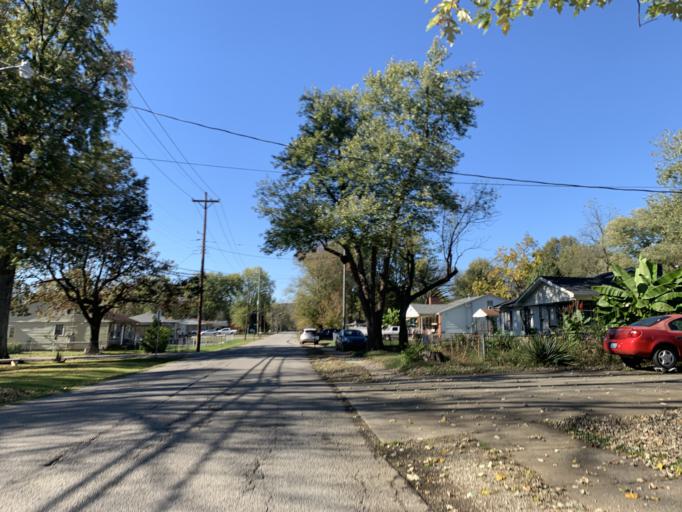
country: US
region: Kentucky
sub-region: Jefferson County
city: Saint Dennis
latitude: 38.1917
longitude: -85.8720
